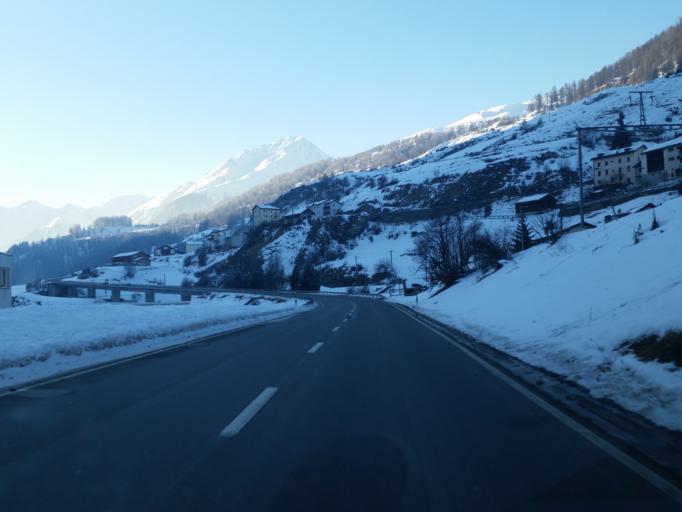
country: CH
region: Grisons
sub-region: Inn District
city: Scuol
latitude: 46.7736
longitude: 10.2002
